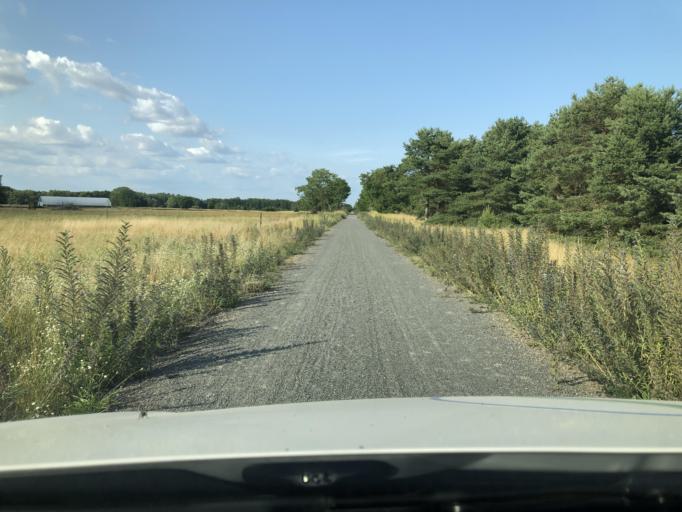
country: SE
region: Skane
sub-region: Kristianstads Kommun
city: Norra Asum
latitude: 55.9374
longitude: 14.1400
